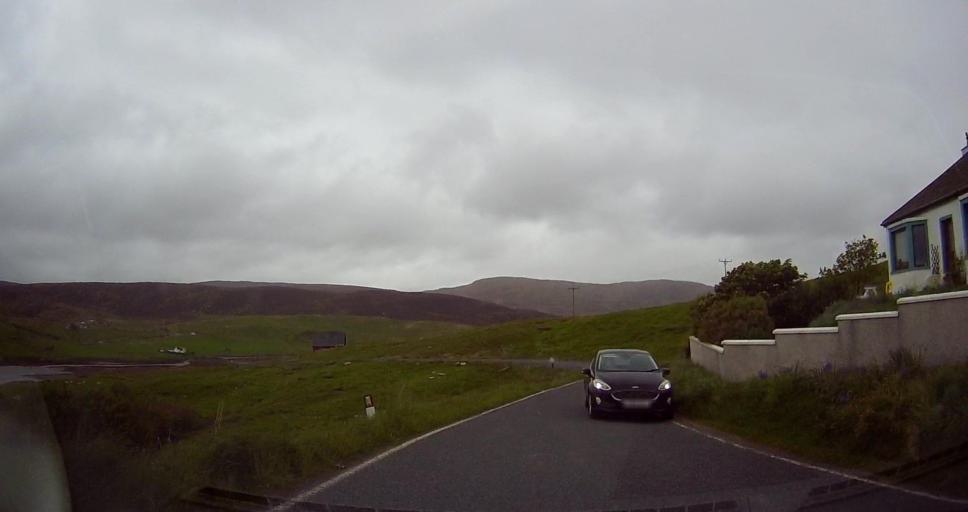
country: GB
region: Scotland
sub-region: Shetland Islands
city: Lerwick
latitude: 60.3019
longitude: -1.3519
